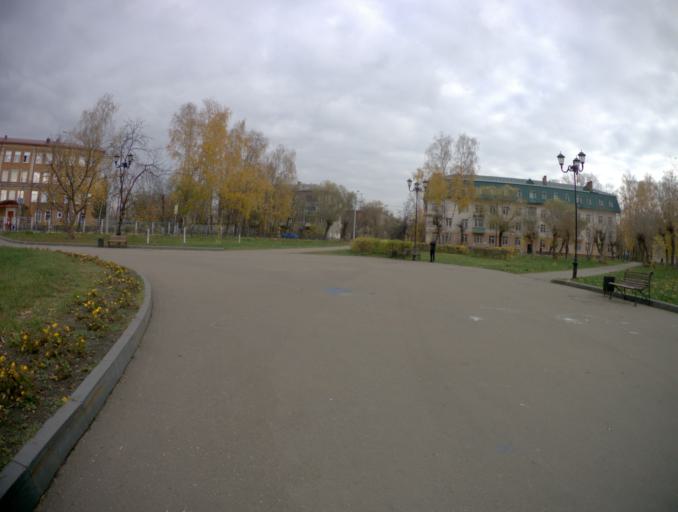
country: RU
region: Moskovskaya
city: Orekhovo-Zuyevo
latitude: 55.8165
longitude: 38.9724
